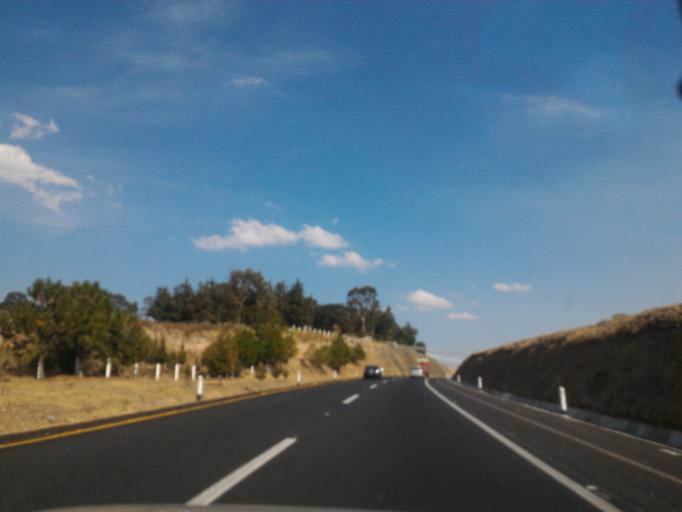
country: MX
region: Mexico
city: Temascalcingo de Jose Maria Velazco
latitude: 19.8547
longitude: -100.0076
